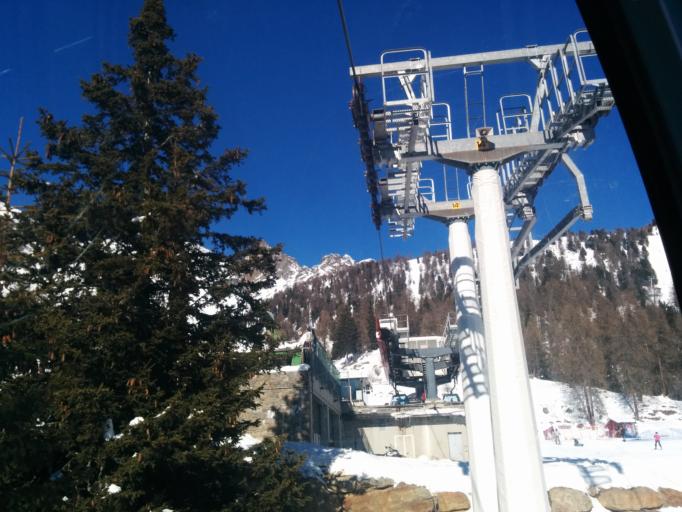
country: IT
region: Trentino-Alto Adige
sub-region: Provincia di Trento
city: Cogolo
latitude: 46.3696
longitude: 10.6603
